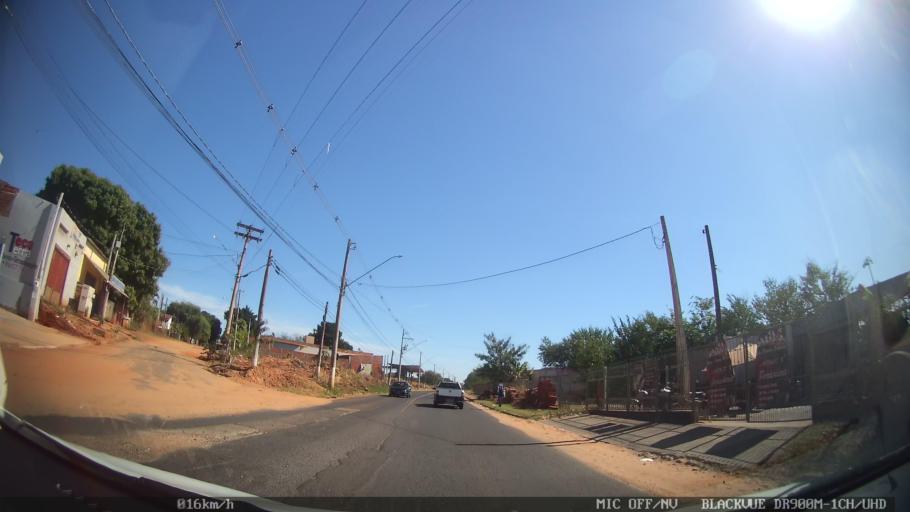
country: BR
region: Sao Paulo
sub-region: Sao Jose Do Rio Preto
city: Sao Jose do Rio Preto
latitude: -20.7631
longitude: -49.4284
